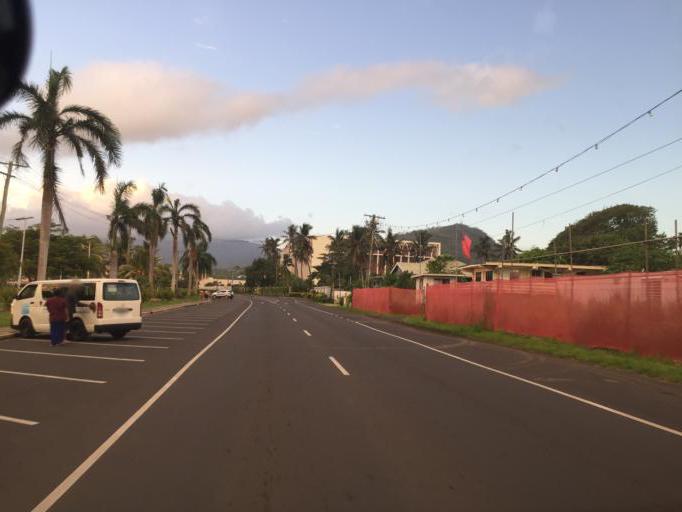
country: WS
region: Tuamasaga
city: Apia
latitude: -13.8264
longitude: -171.7731
